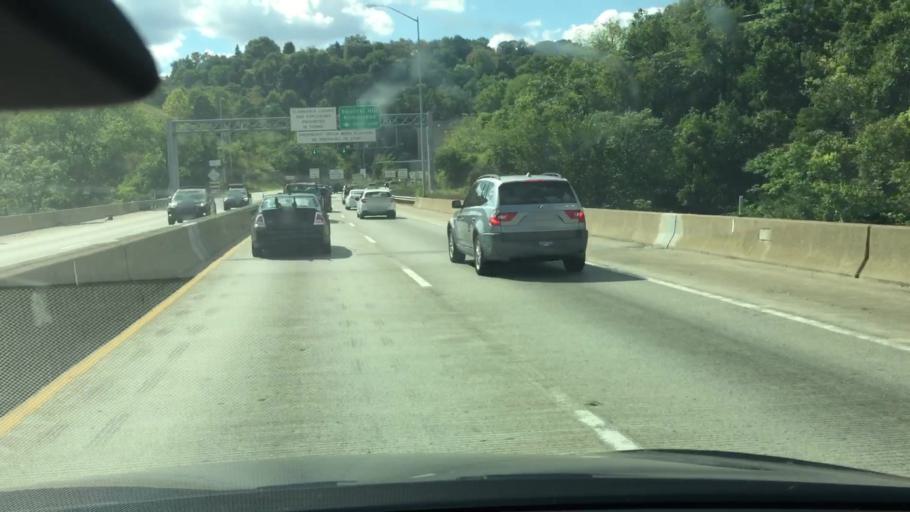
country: US
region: Pennsylvania
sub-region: Allegheny County
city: Homestead
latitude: 40.4263
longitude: -79.9066
